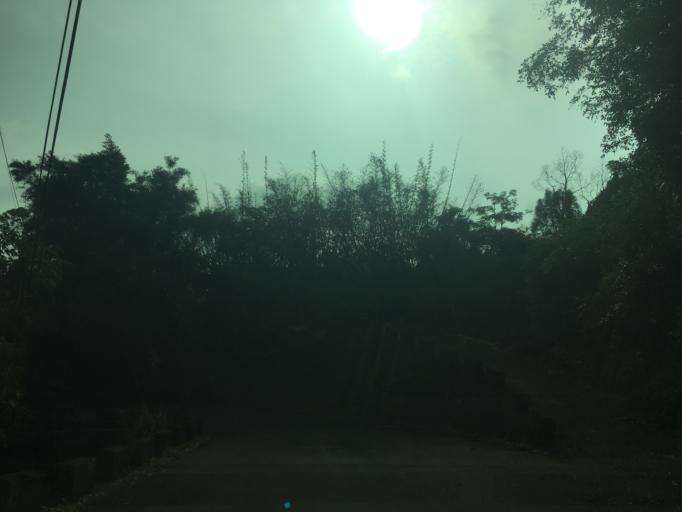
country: TW
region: Taiwan
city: Fengyuan
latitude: 24.2277
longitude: 120.7619
